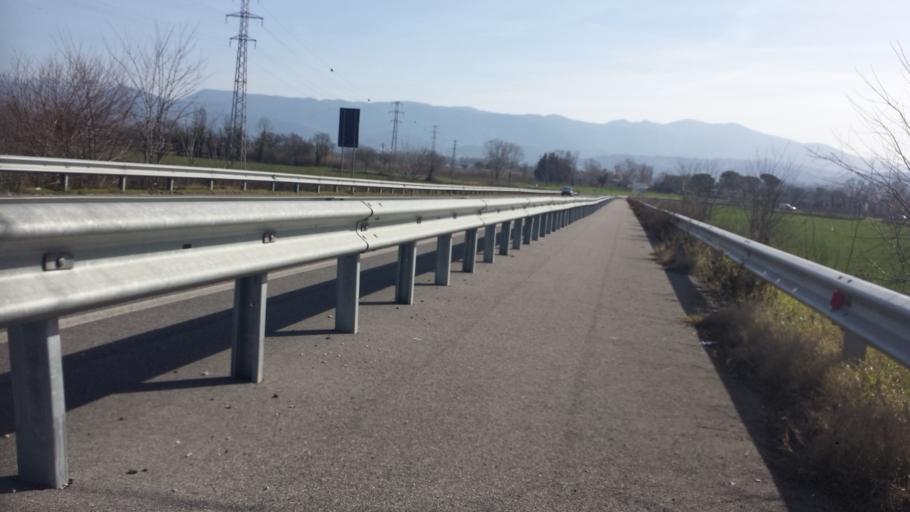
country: IT
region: Umbria
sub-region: Provincia di Terni
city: Terni
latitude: 42.5736
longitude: 12.5992
